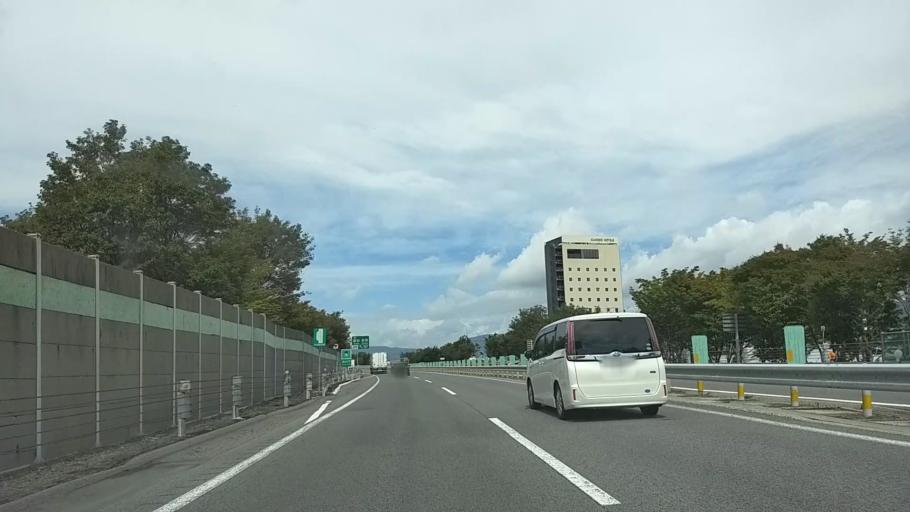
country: JP
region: Nagano
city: Chino
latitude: 35.9999
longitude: 138.1346
